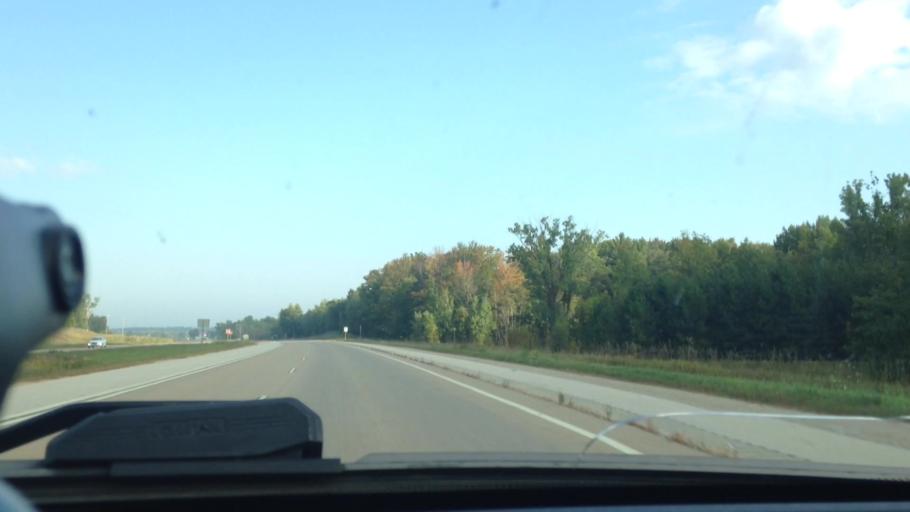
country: US
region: Wisconsin
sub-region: Oconto County
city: Oconto Falls
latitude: 44.9709
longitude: -88.0370
